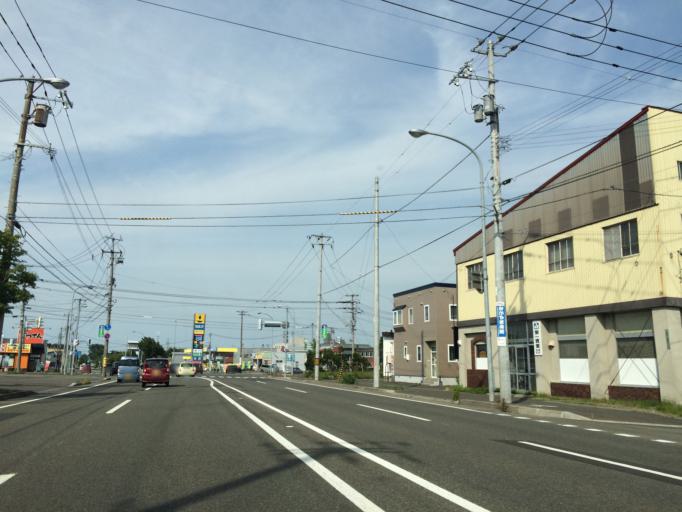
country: JP
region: Hokkaido
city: Ebetsu
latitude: 43.1106
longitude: 141.5486
